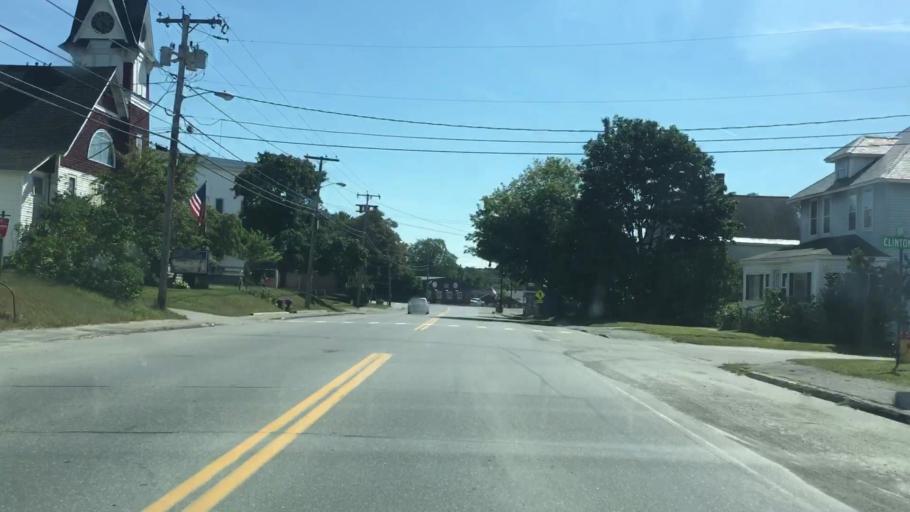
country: US
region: Maine
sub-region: Piscataquis County
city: Milo
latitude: 45.2546
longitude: -68.9866
